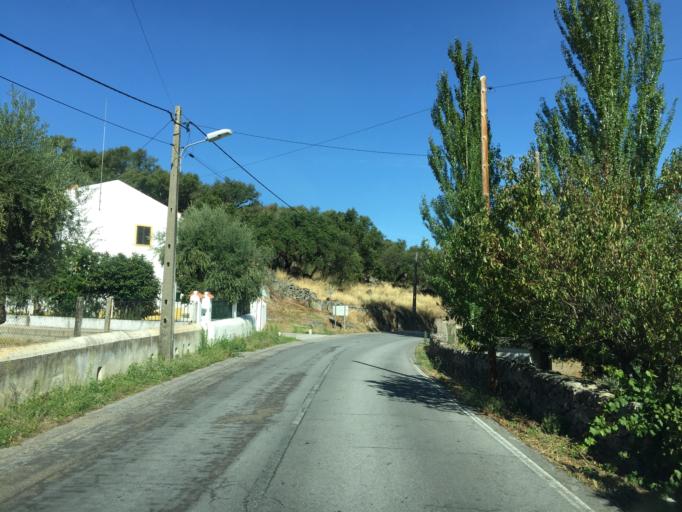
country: PT
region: Portalegre
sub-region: Marvao
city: Marvao
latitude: 39.4181
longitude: -7.3522
